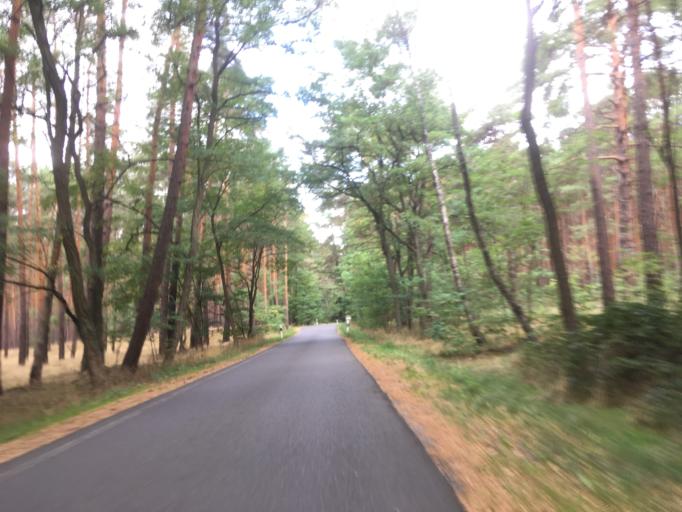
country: DE
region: Brandenburg
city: Bestensee
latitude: 52.2531
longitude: 13.7662
